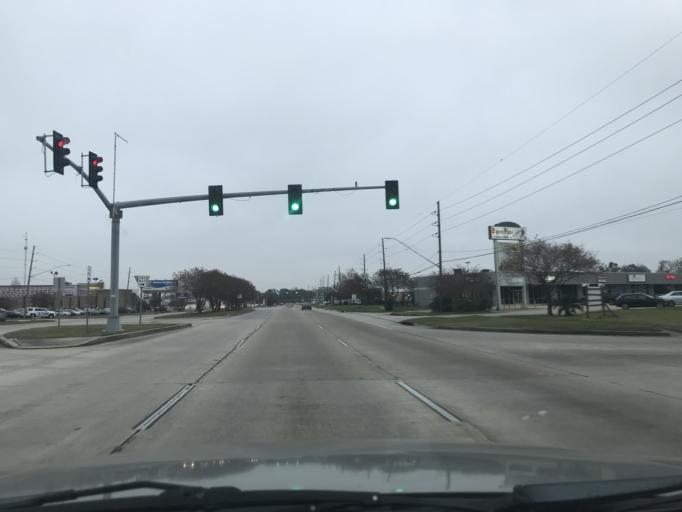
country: US
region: Louisiana
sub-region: Jefferson Parish
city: Woodmere
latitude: 29.8741
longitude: -90.0891
